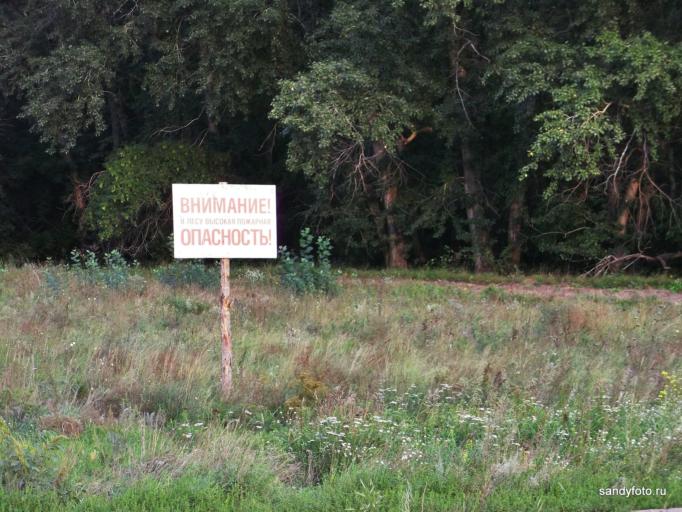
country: RU
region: Chelyabinsk
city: Troitsk
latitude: 54.0606
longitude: 61.6250
